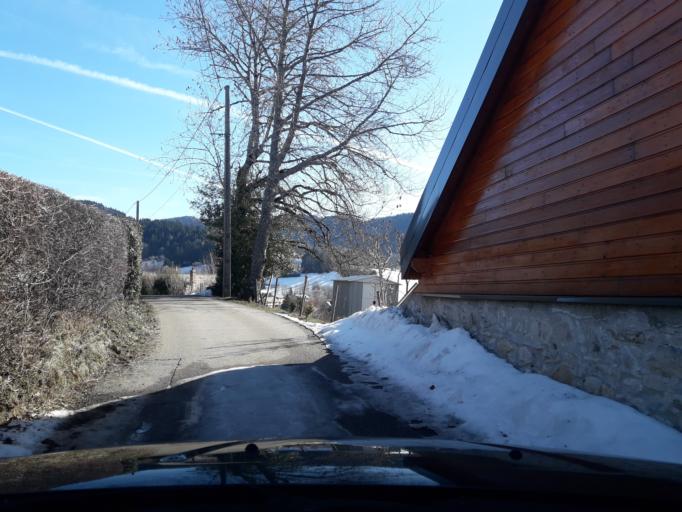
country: FR
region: Rhone-Alpes
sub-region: Departement de l'Isere
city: Le Sappey-en-Chartreuse
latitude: 45.2643
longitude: 5.7744
